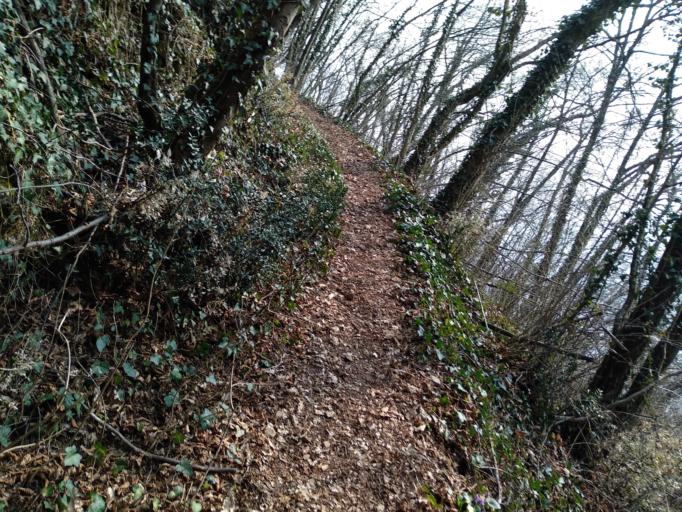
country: IT
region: Veneto
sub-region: Provincia di Vicenza
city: Santorso
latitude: 45.7484
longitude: 11.4061
